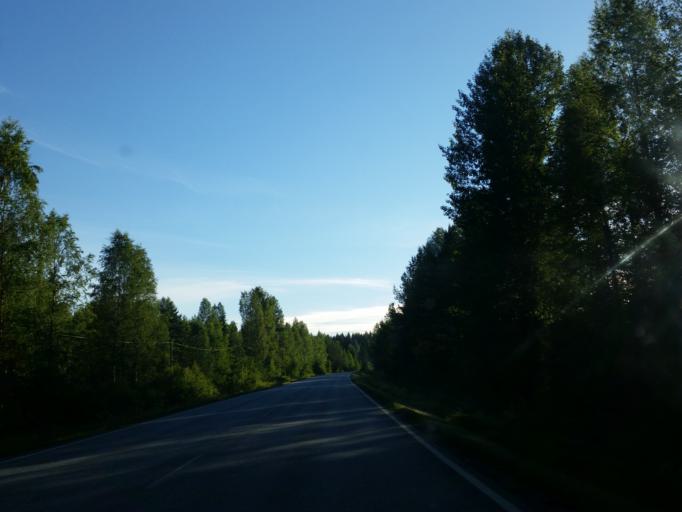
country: FI
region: Northern Savo
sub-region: Kuopio
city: Karttula
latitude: 62.8578
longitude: 27.2247
